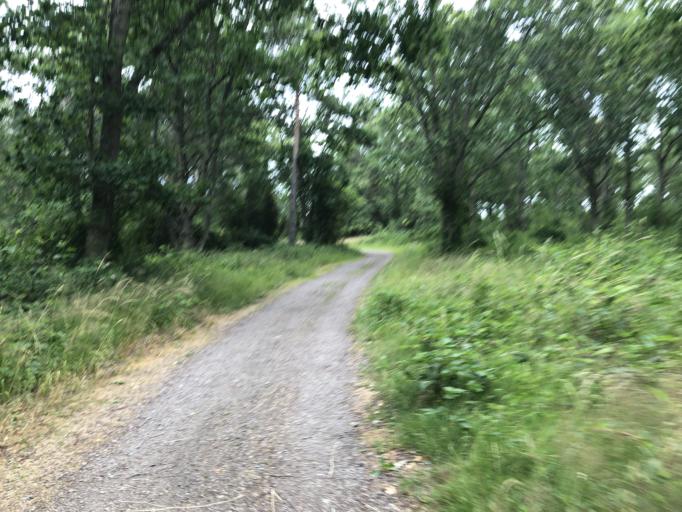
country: SE
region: Kalmar
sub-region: Kalmar Kommun
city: Kalmar
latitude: 56.6350
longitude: 16.3197
